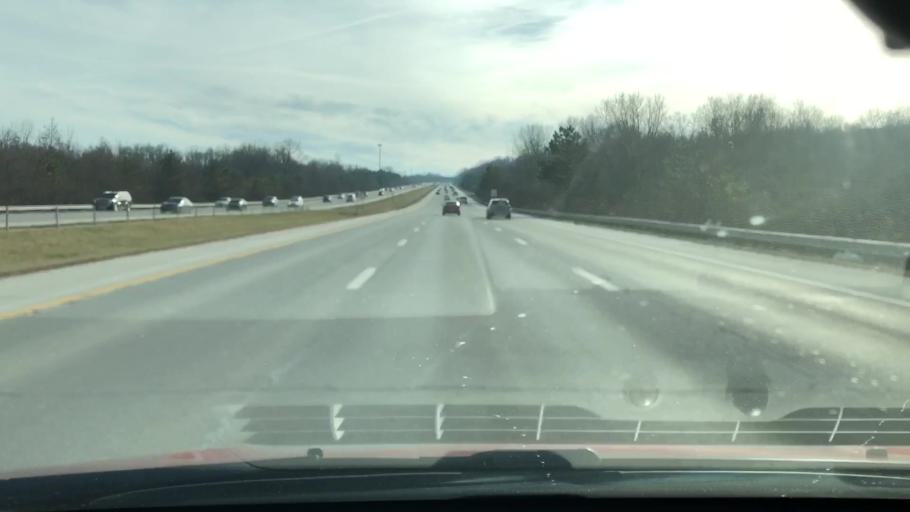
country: US
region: Ohio
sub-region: Greene County
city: Beavercreek
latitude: 39.7240
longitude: -84.0911
